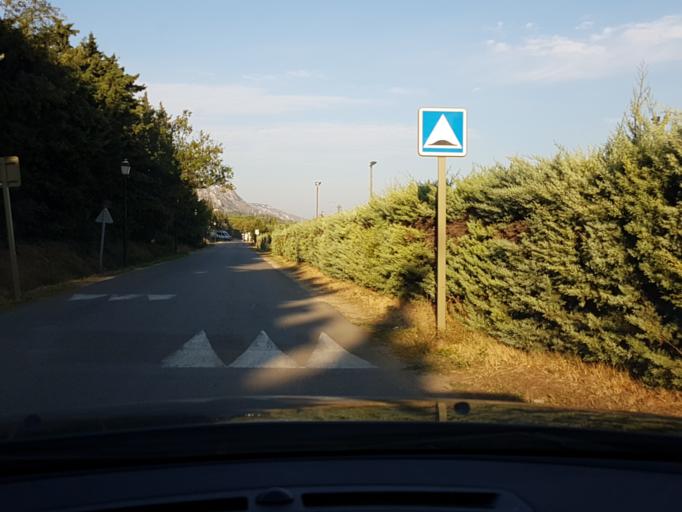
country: FR
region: Provence-Alpes-Cote d'Azur
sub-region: Departement des Bouches-du-Rhone
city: Eygalieres
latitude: 43.7606
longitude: 4.9471
